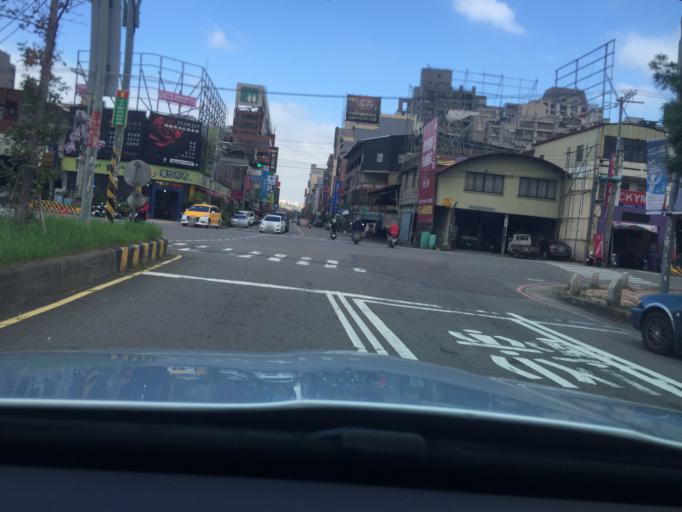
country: TW
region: Taiwan
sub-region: Hsinchu
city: Zhubei
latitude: 24.8241
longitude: 121.0080
